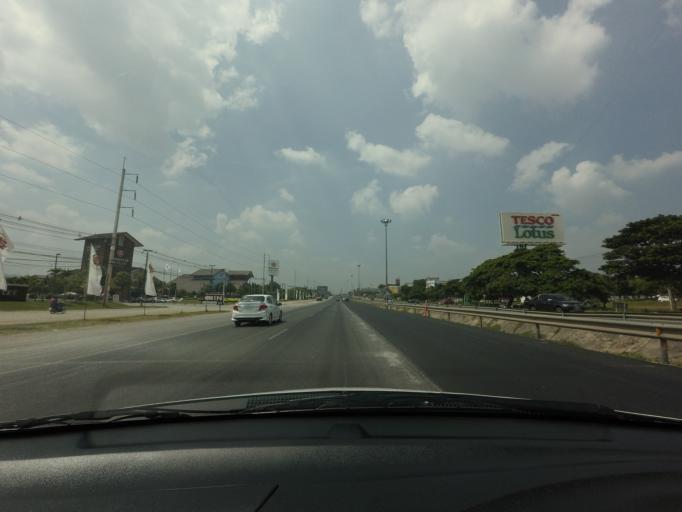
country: TH
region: Nakhon Ratchasima
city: Pak Chong
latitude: 14.6608
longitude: 101.3938
